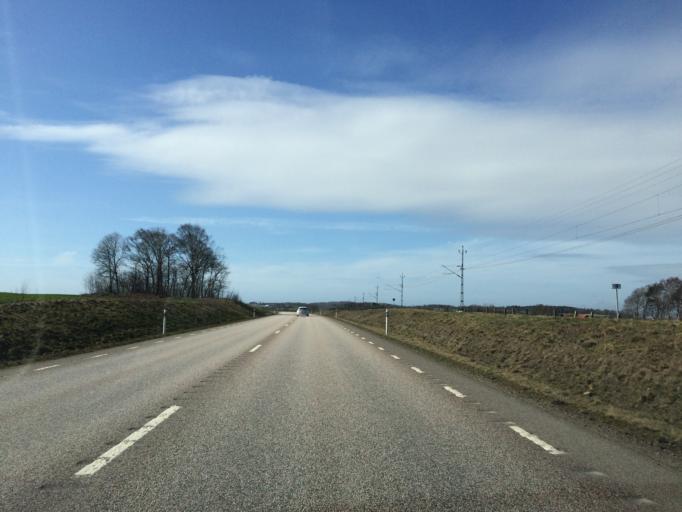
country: SE
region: Halland
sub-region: Laholms Kommun
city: Veinge
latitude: 56.5423
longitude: 13.1365
